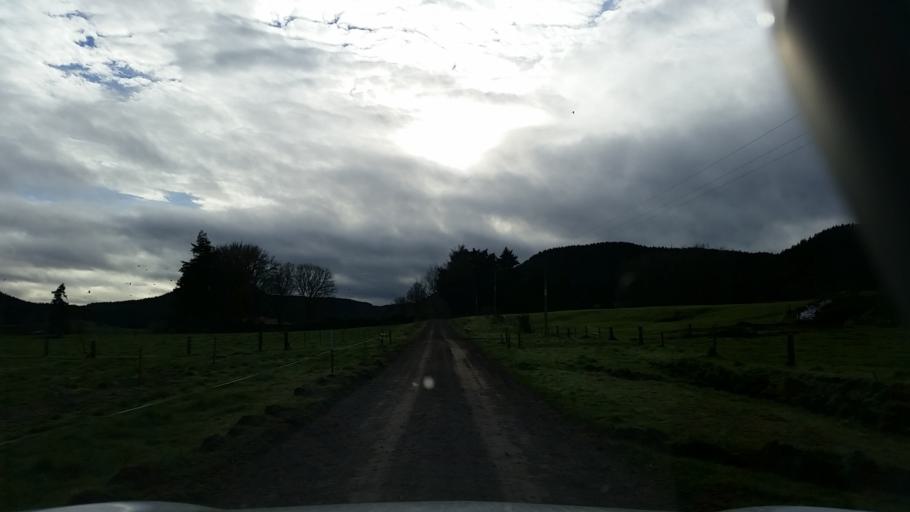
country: NZ
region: Bay of Plenty
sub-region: Rotorua District
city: Rotorua
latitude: -38.3937
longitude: 176.3914
